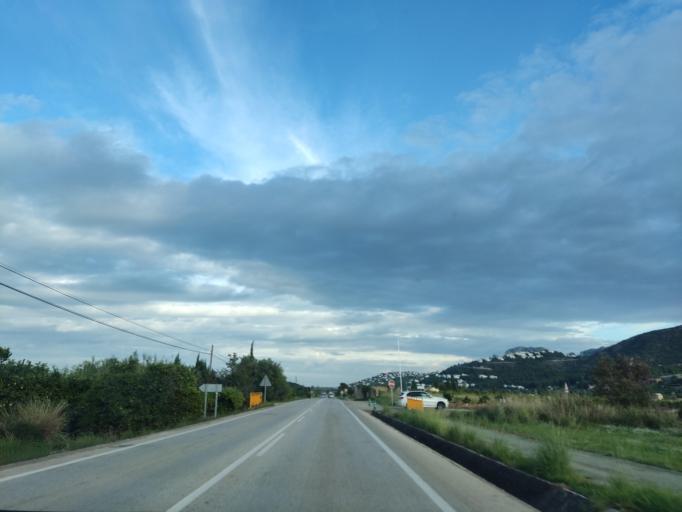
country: ES
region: Valencia
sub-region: Provincia de Alicante
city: Pego
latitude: 38.8468
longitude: -0.0882
